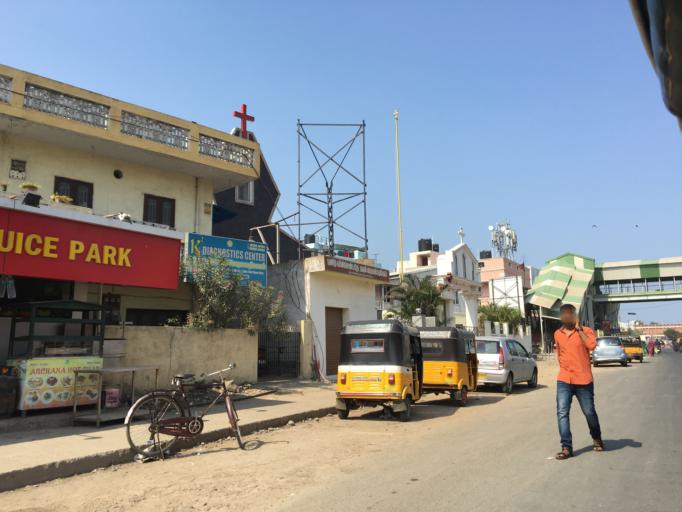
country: IN
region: Tamil Nadu
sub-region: Kancheepuram
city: Perungudi
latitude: 12.9814
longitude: 80.2418
